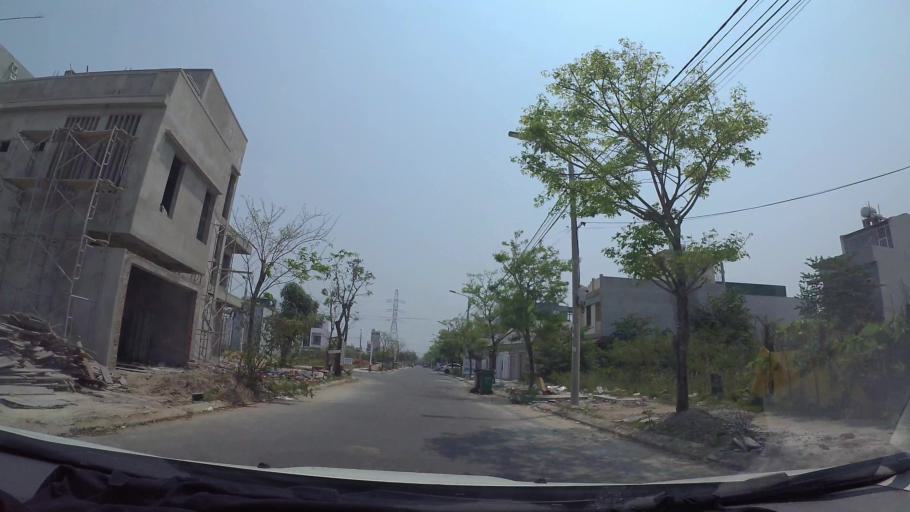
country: VN
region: Da Nang
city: Cam Le
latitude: 16.0118
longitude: 108.2207
